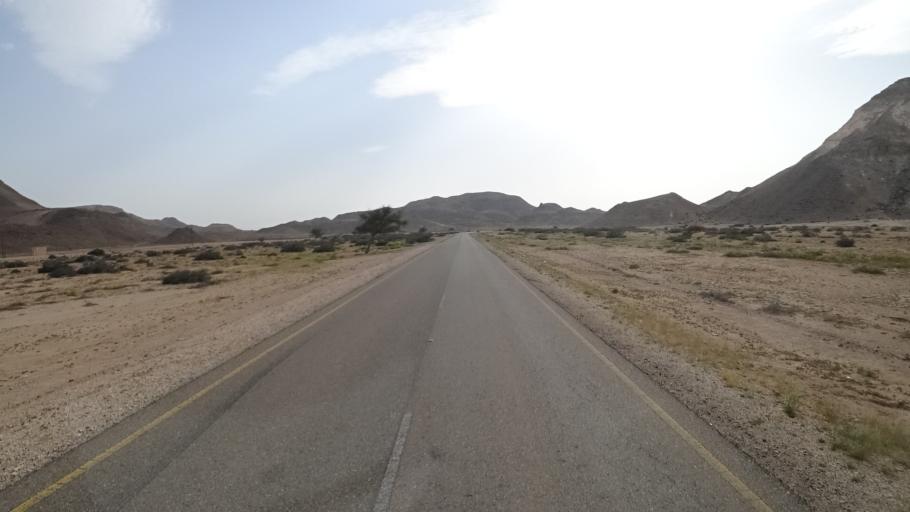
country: OM
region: Ash Sharqiyah
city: Sur
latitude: 22.4350
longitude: 59.8174
